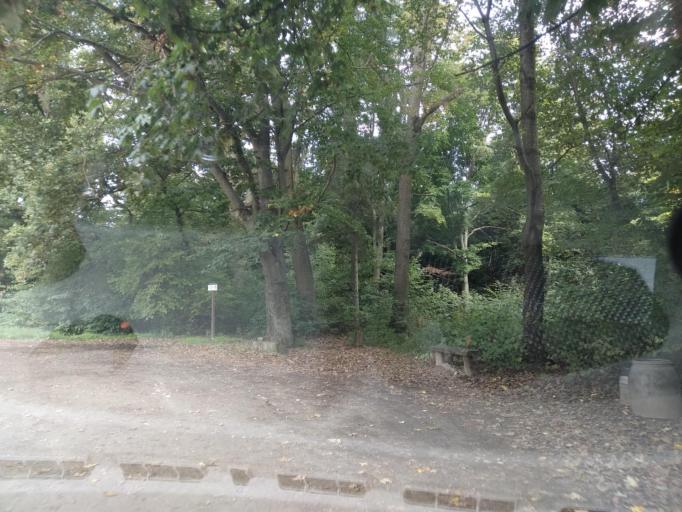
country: PL
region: Subcarpathian Voivodeship
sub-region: Powiat jasielski
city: Tarnowiec
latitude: 49.7862
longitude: 21.5596
